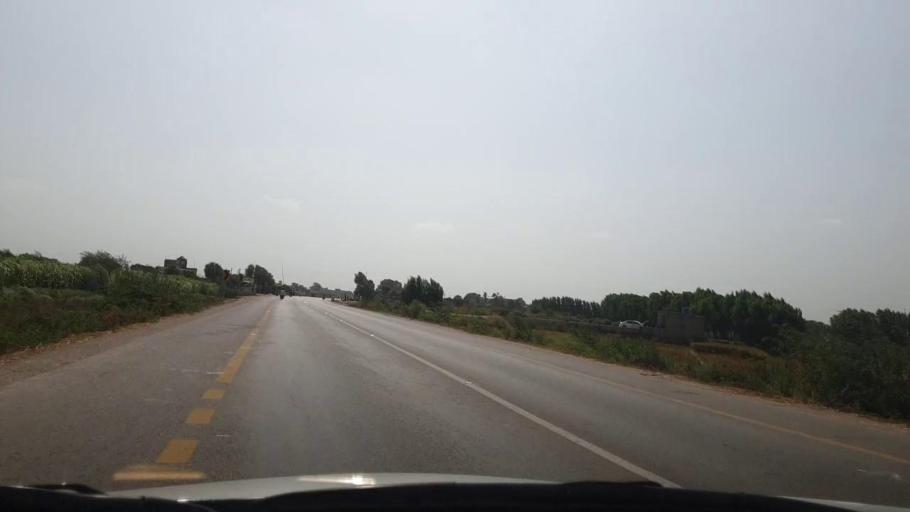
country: PK
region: Sindh
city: Matli
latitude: 25.0702
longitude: 68.6236
